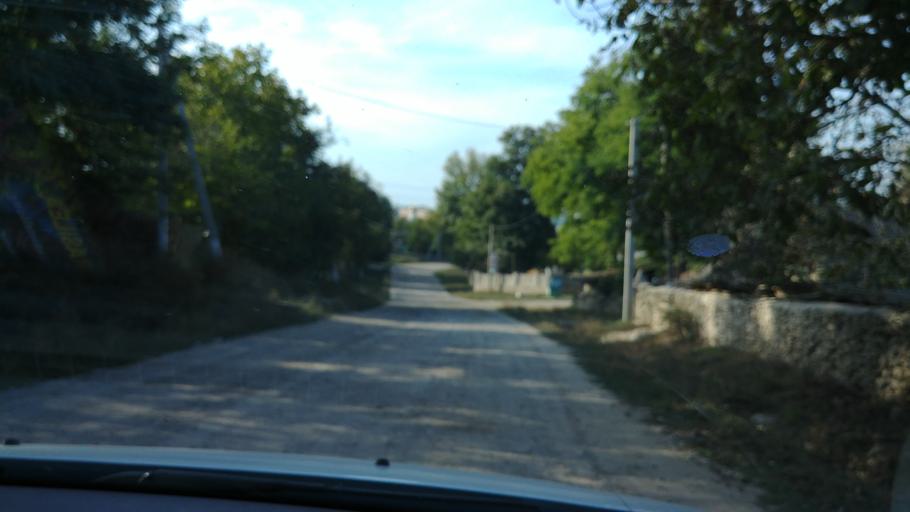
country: MD
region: Rezina
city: Rezina
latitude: 47.7466
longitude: 28.8867
